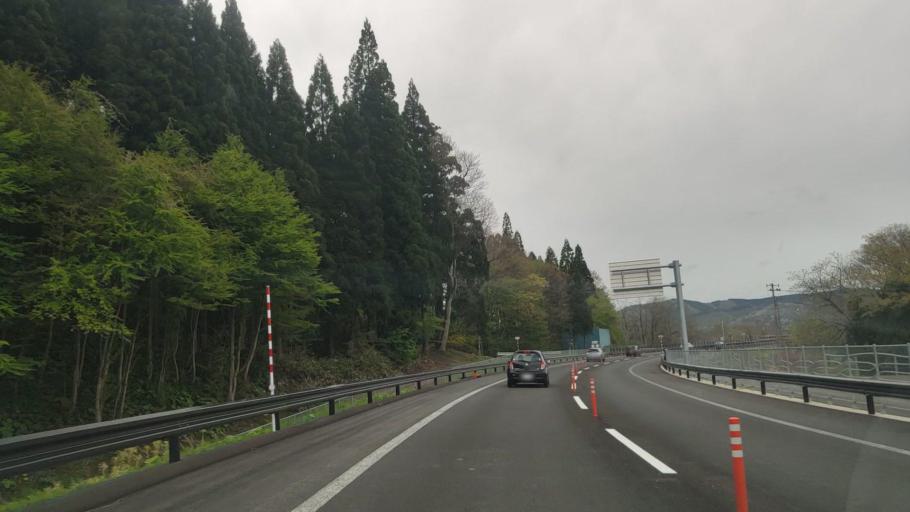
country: JP
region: Akita
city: Takanosu
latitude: 40.2048
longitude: 140.3070
